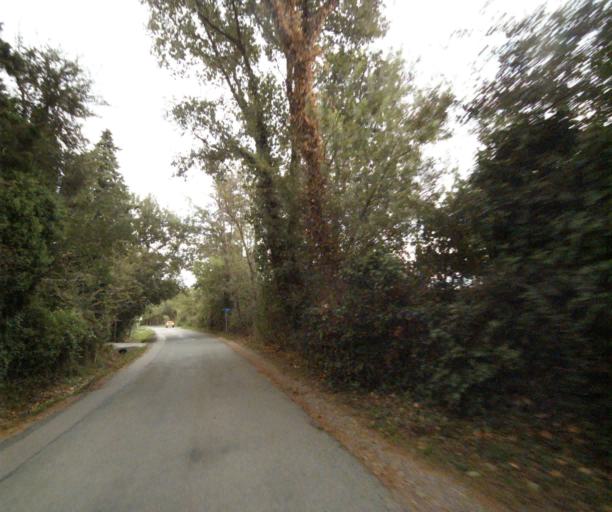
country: FR
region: Languedoc-Roussillon
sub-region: Departement des Pyrenees-Orientales
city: Argelers
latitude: 42.5659
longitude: 3.0323
